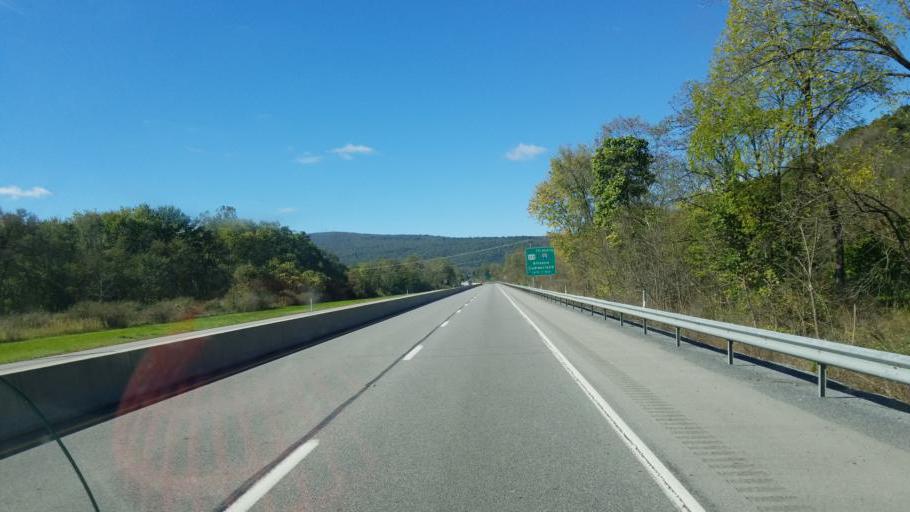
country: US
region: Pennsylvania
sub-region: Bedford County
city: Bedford
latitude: 40.0205
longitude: -78.4908
